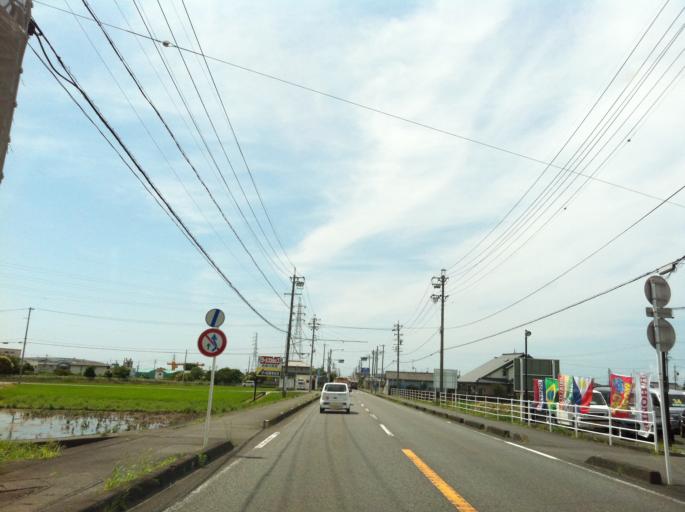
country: JP
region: Shizuoka
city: Shimada
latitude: 34.7895
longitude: 138.2534
